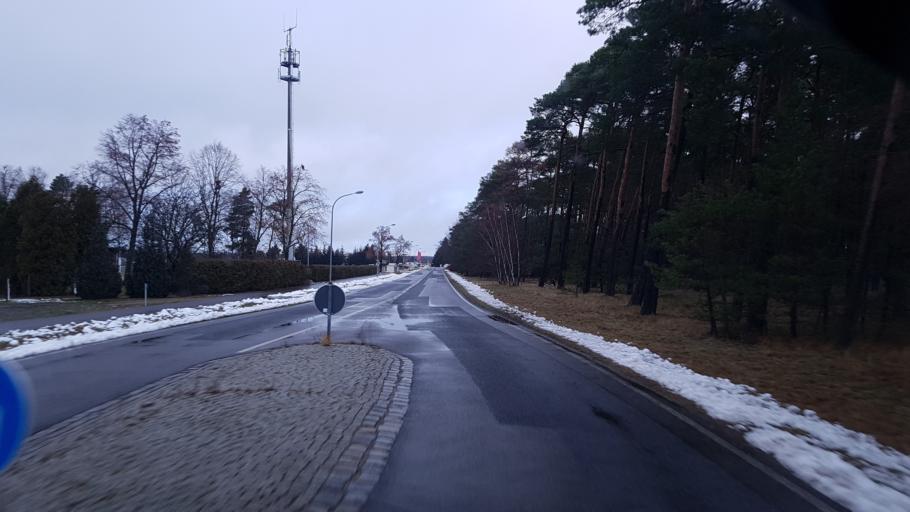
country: DE
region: Brandenburg
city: Janschwalde
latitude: 51.8567
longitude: 14.5051
